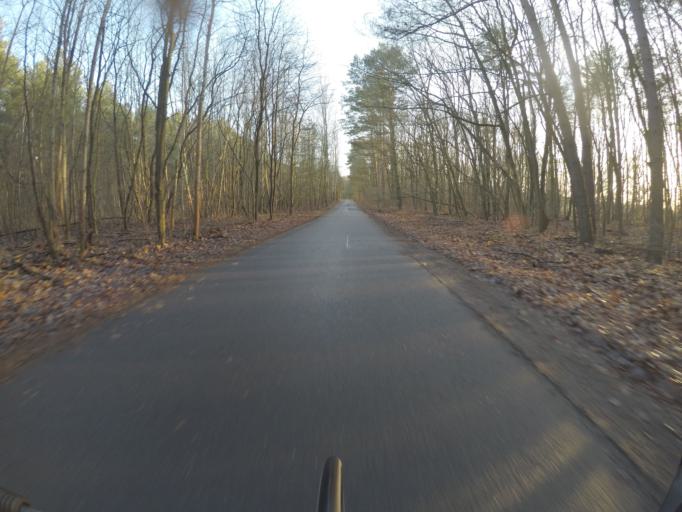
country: DE
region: Brandenburg
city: Hennigsdorf
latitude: 52.6501
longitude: 13.2258
